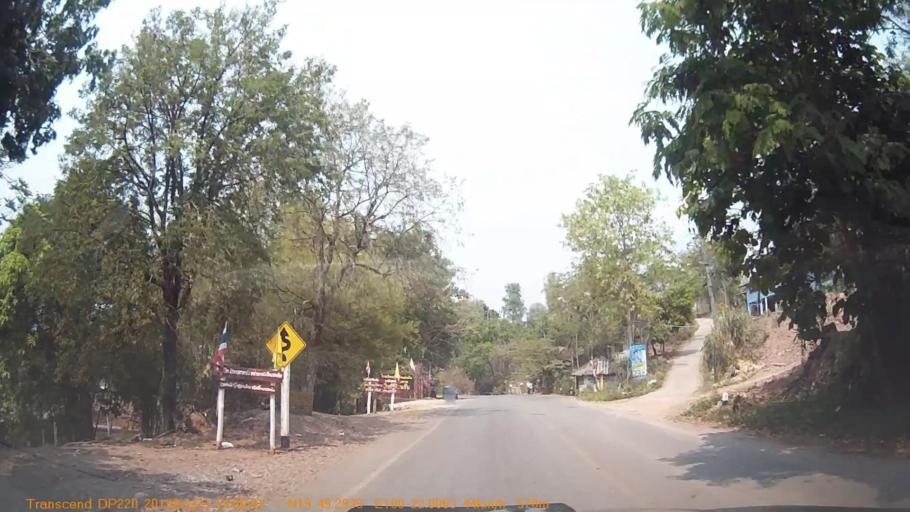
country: TH
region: Chiang Rai
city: Khun Tan
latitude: 19.8217
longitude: 100.3669
